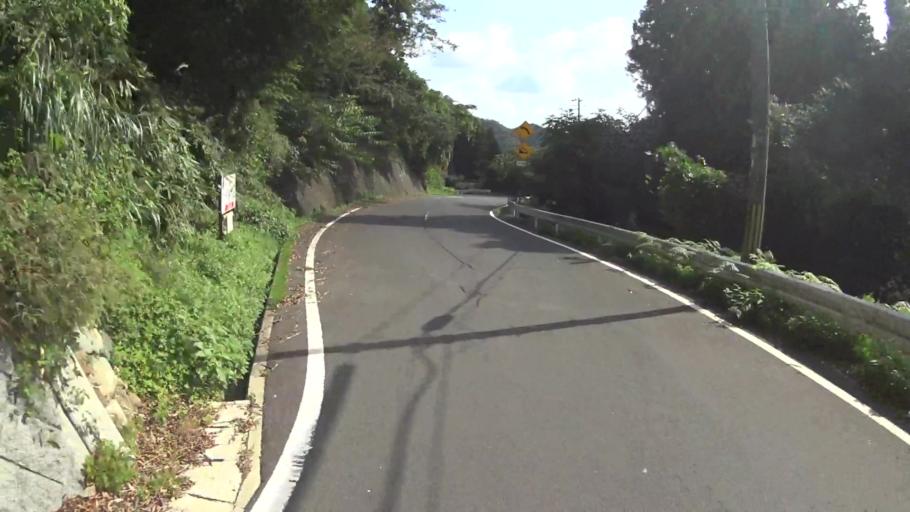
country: JP
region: Kyoto
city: Miyazu
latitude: 35.6348
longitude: 135.1993
